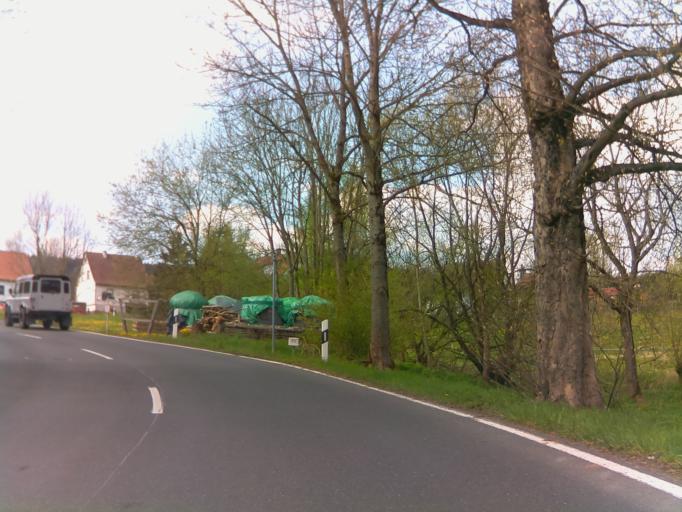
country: DE
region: Bavaria
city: Foritz
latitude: 50.3667
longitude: 11.2405
